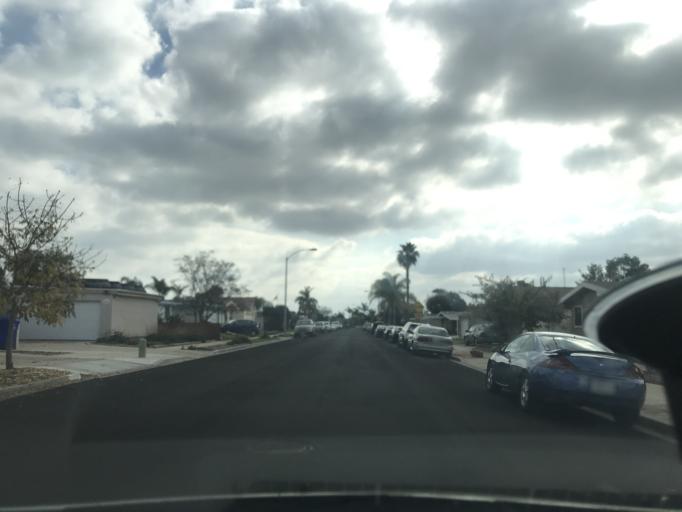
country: US
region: California
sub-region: San Diego County
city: San Diego
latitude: 32.7998
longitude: -117.1362
